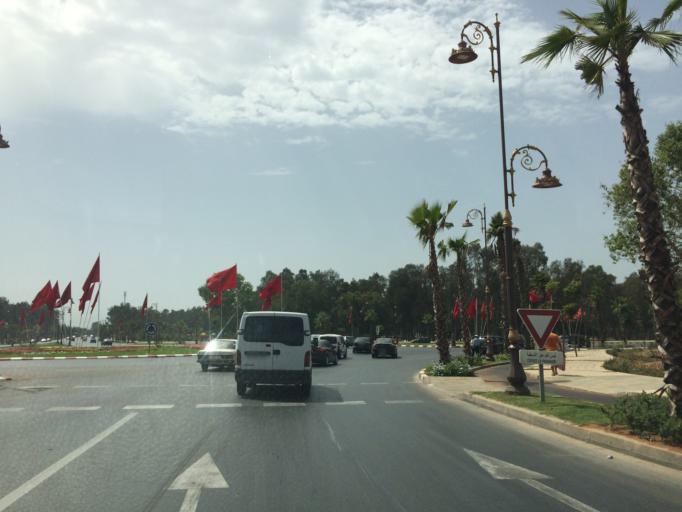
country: MA
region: Rabat-Sale-Zemmour-Zaer
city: Sale
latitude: 34.0332
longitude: -6.7748
